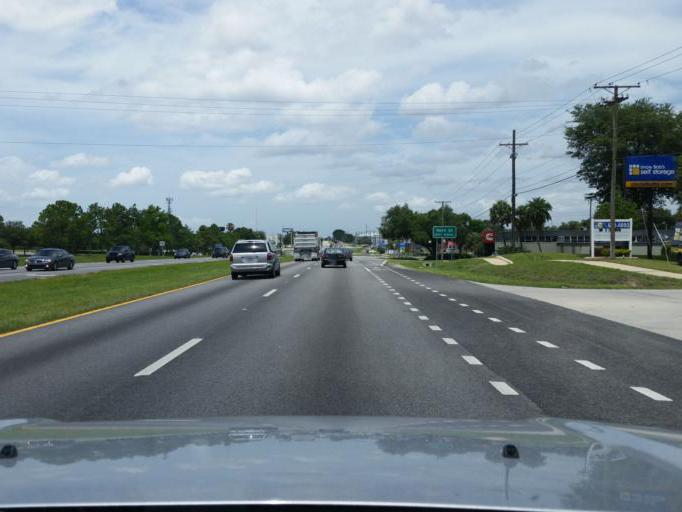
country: US
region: Florida
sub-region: Hillsborough County
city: East Lake-Orient Park
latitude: 27.9963
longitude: -82.3876
